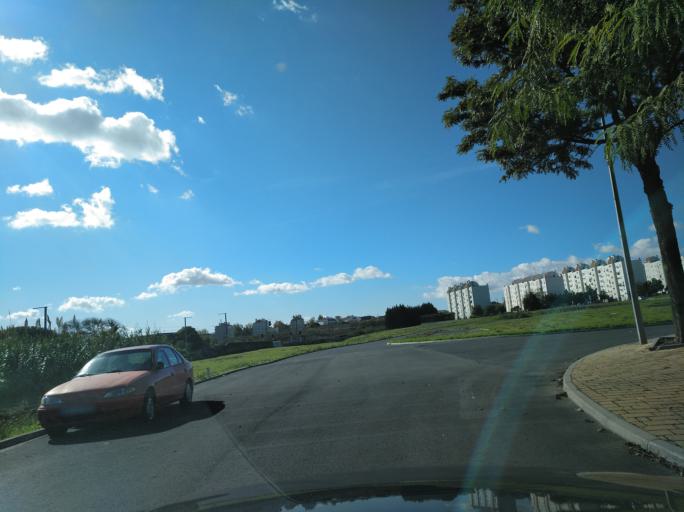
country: PT
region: Lisbon
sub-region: Lisbon
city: Lisbon
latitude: 38.7395
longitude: -9.1091
